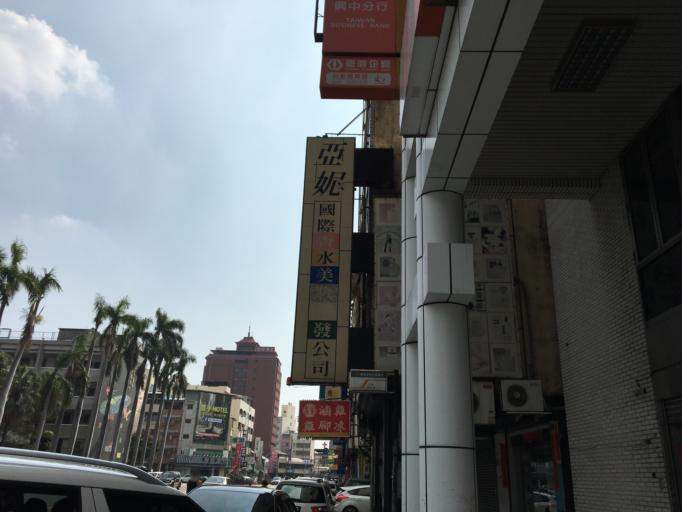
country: TW
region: Taiwan
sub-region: Taichung City
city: Taichung
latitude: 24.1317
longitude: 120.6842
